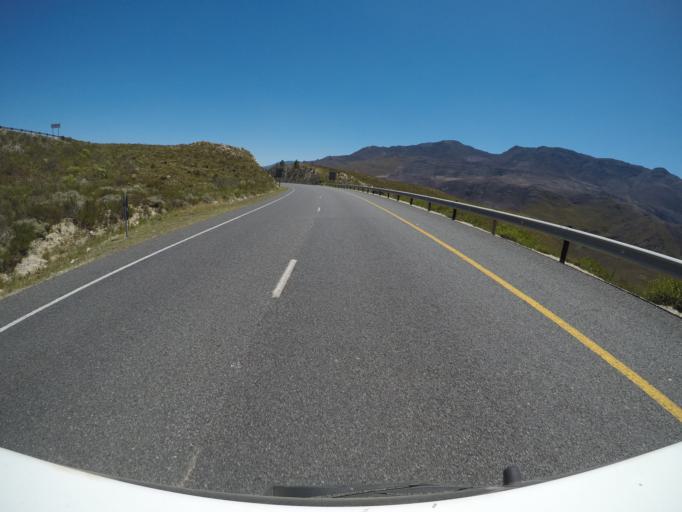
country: ZA
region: Western Cape
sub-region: Overberg District Municipality
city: Grabouw
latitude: -34.2173
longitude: 19.1736
